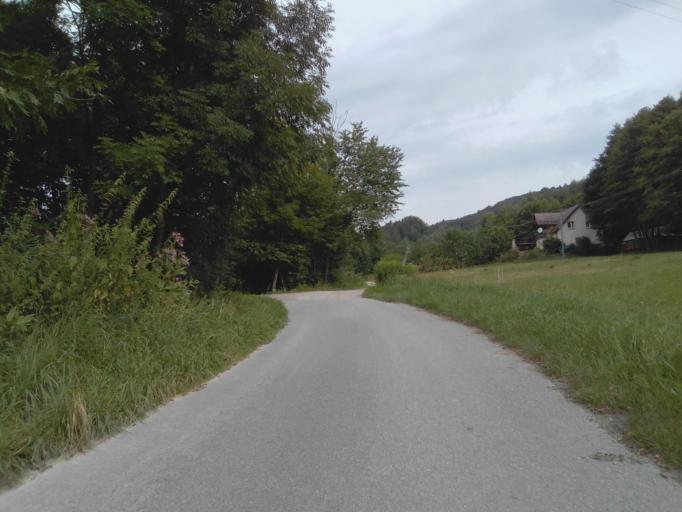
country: PL
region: Subcarpathian Voivodeship
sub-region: Powiat strzyzowski
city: Frysztak
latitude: 49.8744
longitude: 21.5663
